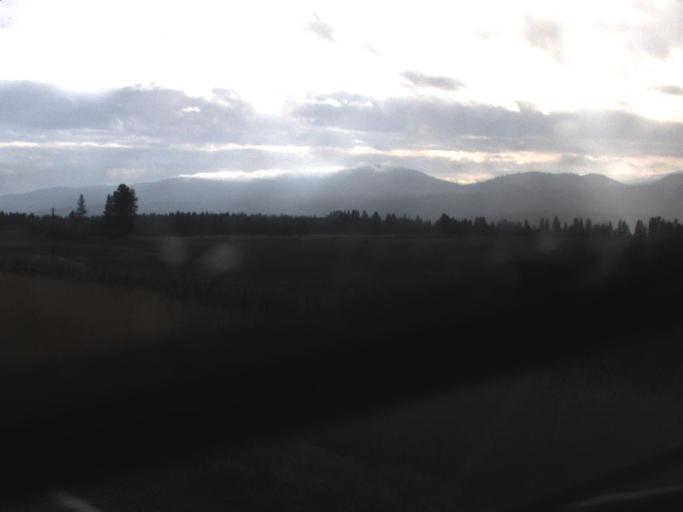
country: US
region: Washington
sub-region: Stevens County
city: Kettle Falls
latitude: 48.4620
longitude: -118.1802
